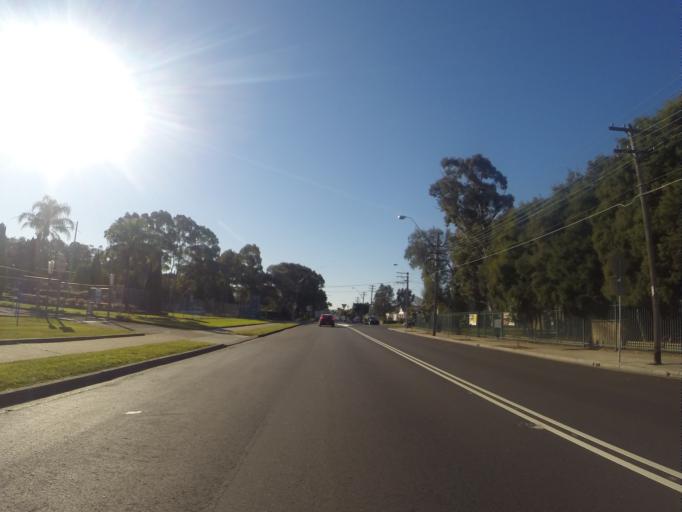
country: AU
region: New South Wales
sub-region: Auburn
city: Auburn
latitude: -33.8604
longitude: 151.0191
